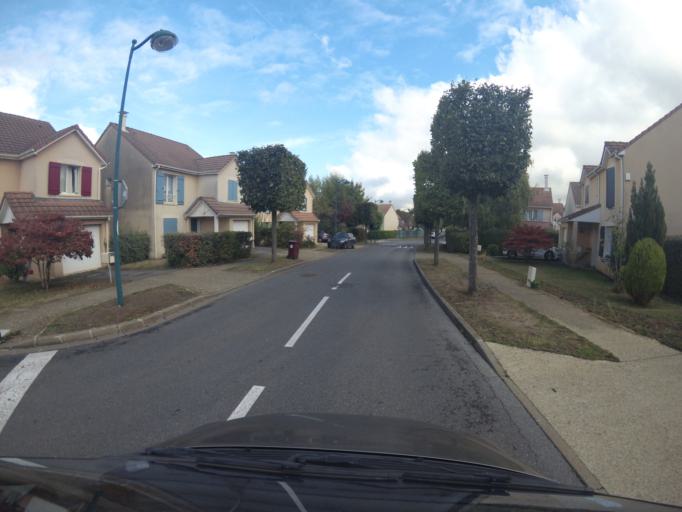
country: FR
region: Ile-de-France
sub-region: Departement de Seine-et-Marne
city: Montevrain
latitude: 48.8688
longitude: 2.7461
